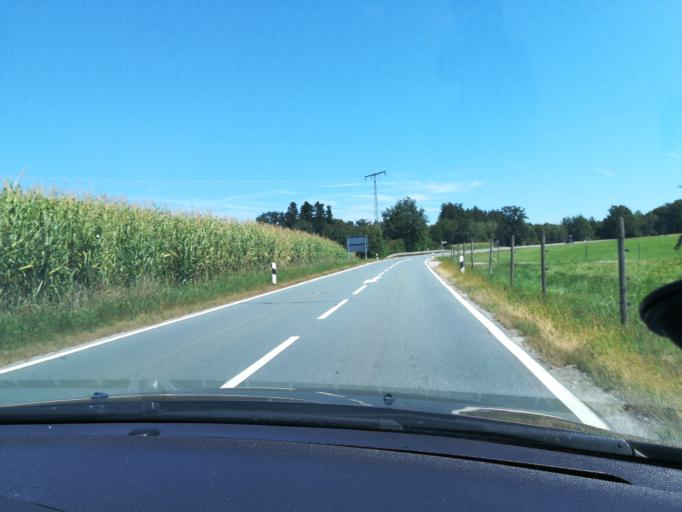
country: DE
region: Bavaria
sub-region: Upper Bavaria
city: Amerang
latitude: 48.0206
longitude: 12.2922
